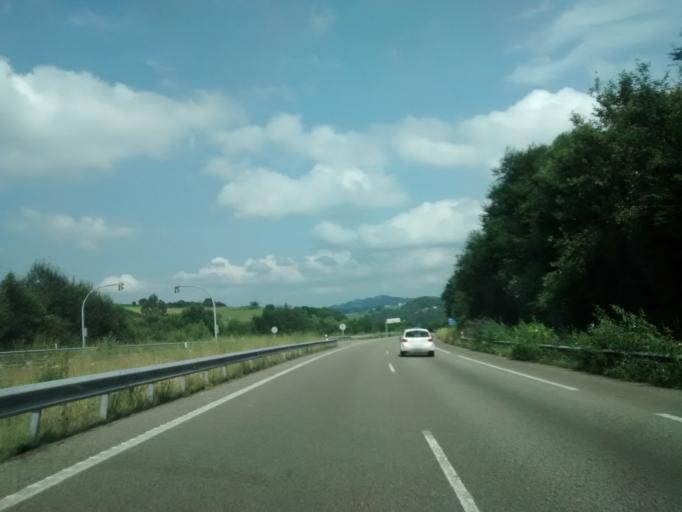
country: ES
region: Asturias
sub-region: Province of Asturias
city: Norena
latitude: 43.3445
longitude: -5.6969
